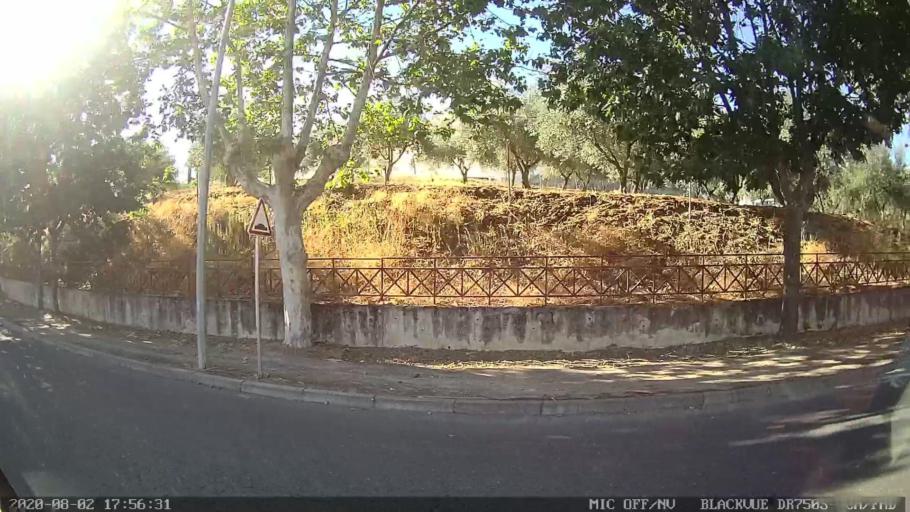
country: PT
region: Vila Real
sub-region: Murca
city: Murca
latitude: 41.4007
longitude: -7.4560
